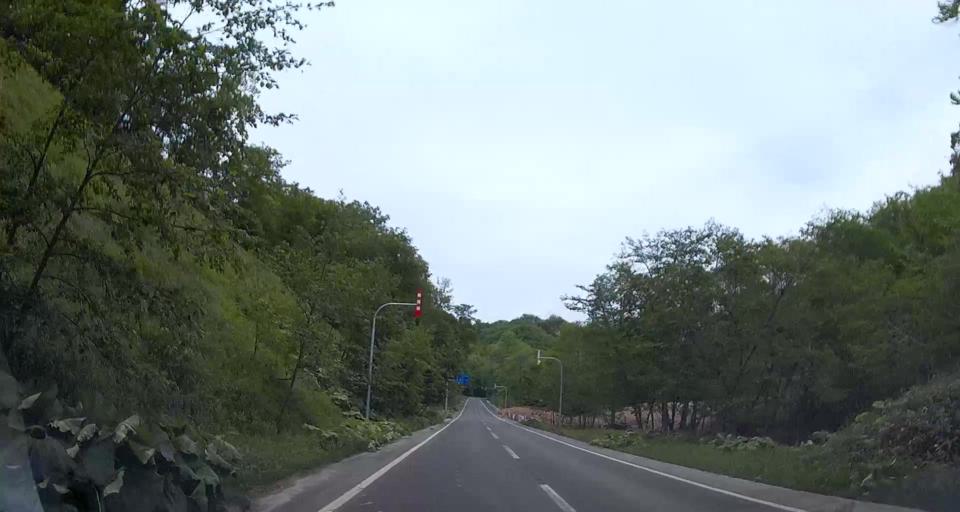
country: JP
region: Hokkaido
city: Chitose
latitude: 42.7903
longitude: 142.0520
